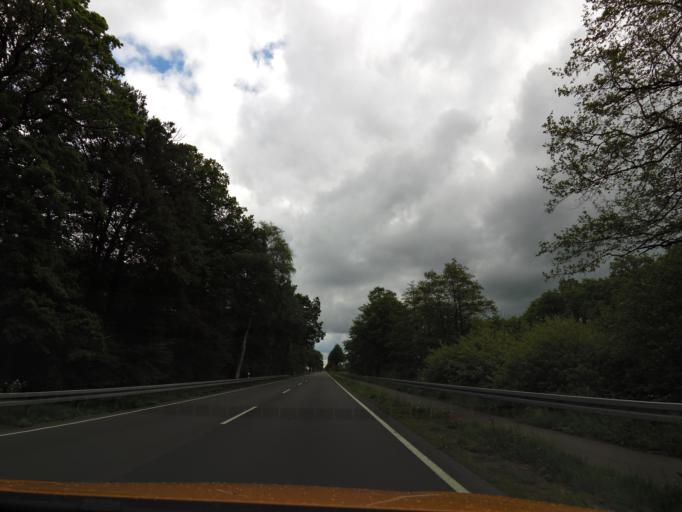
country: DE
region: Lower Saxony
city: Twistringen
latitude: 52.8209
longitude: 8.6789
